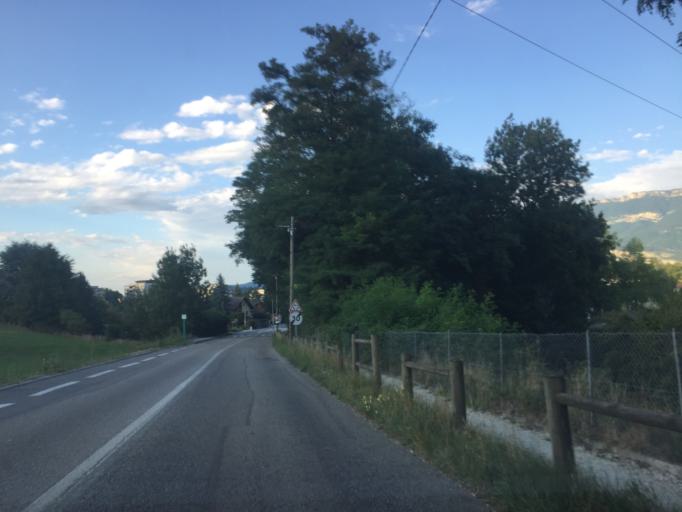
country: FR
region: Rhone-Alpes
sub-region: Departement de la Savoie
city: La Motte-Servolex
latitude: 45.5899
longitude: 5.8698
